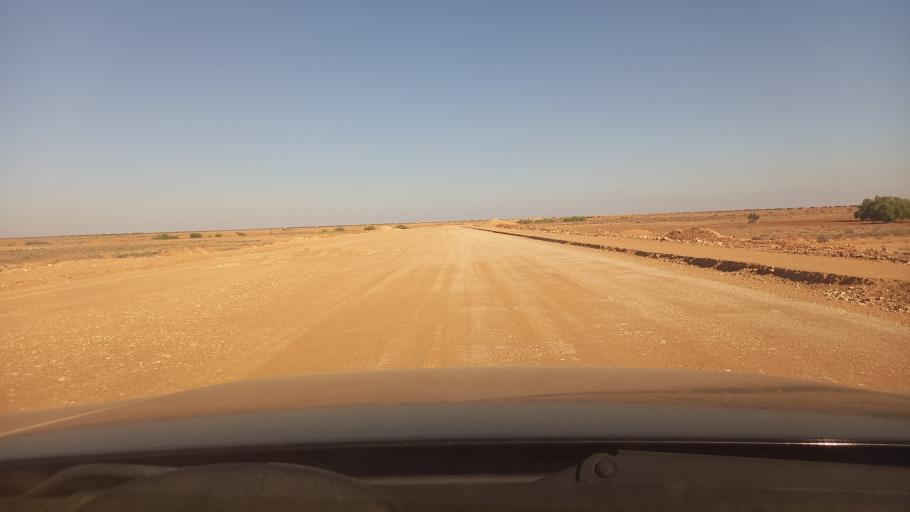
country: TN
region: Madanin
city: Medenine
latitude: 33.1412
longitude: 10.5057
